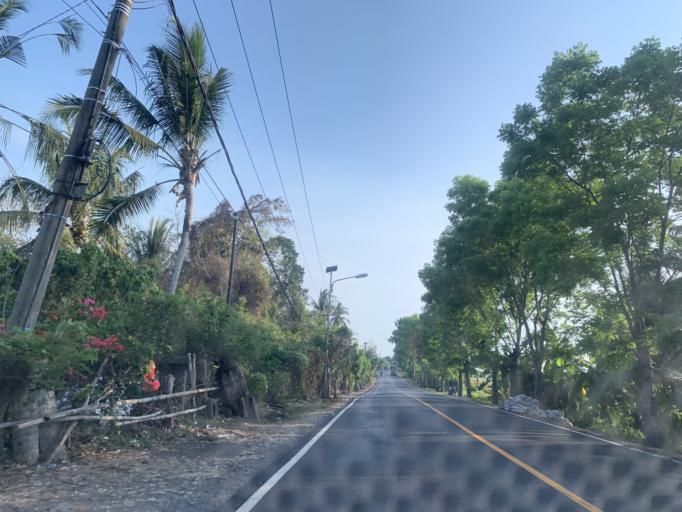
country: ID
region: Bali
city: Banjar Delodrurung
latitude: -8.5107
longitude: 115.0171
